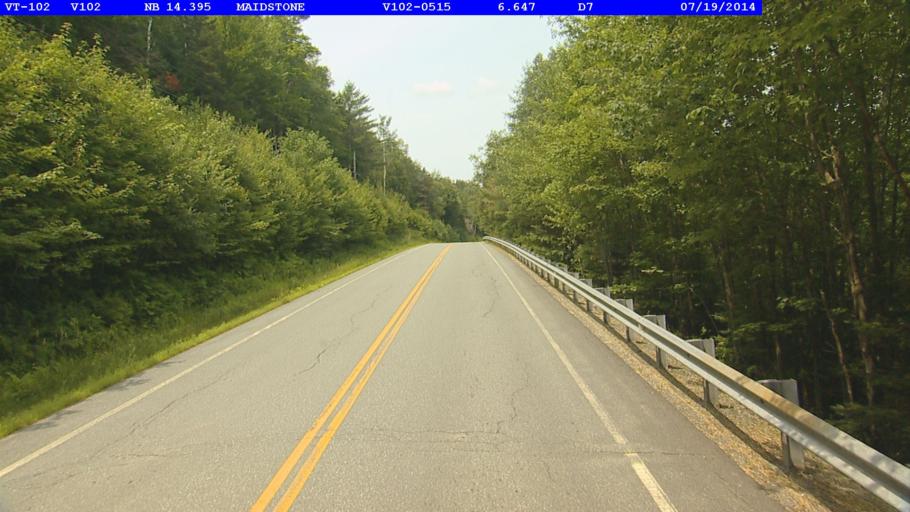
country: US
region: New Hampshire
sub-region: Coos County
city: Stratford
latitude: 44.6501
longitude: -71.5783
